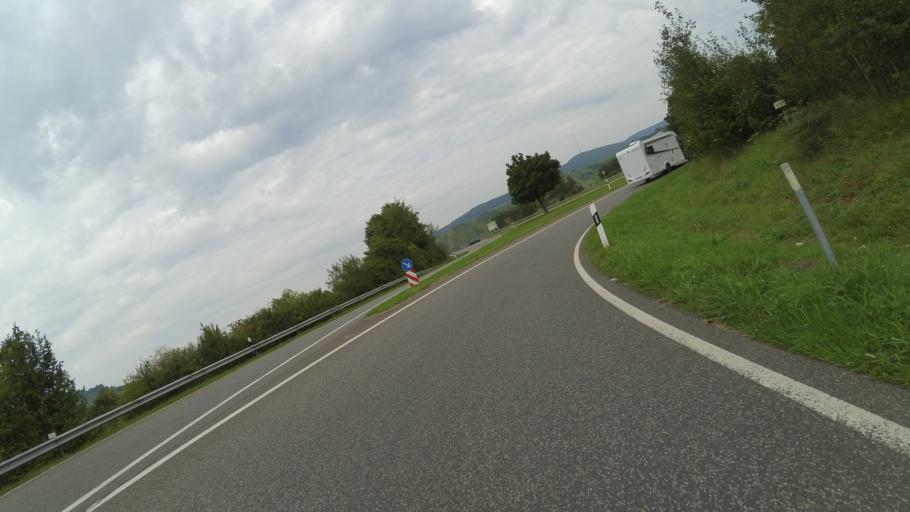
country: DE
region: Rheinland-Pfalz
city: Ockfen
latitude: 49.6080
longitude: 6.5664
